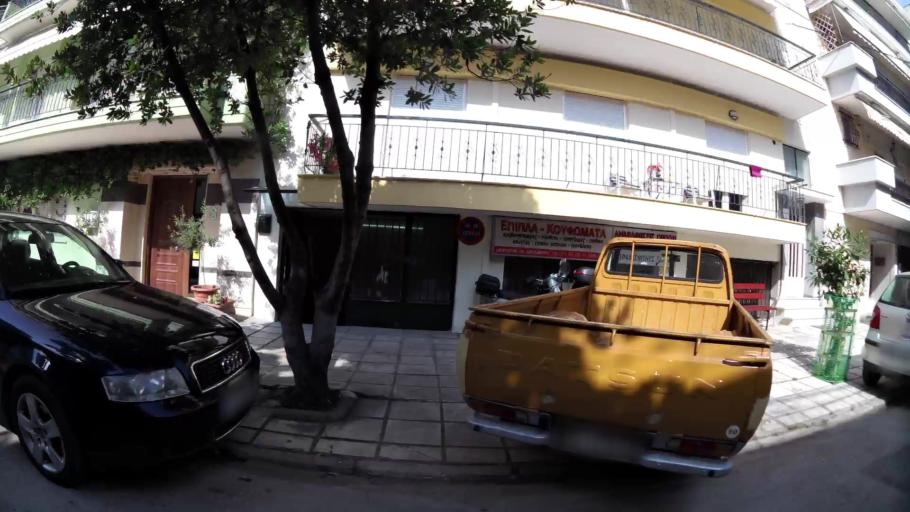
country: GR
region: Central Macedonia
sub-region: Nomos Thessalonikis
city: Stavroupoli
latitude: 40.6710
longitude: 22.9272
